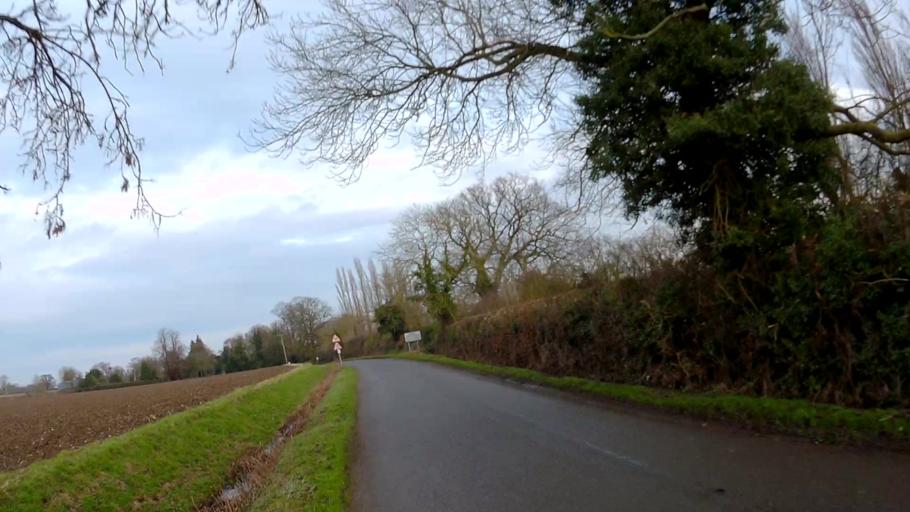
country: GB
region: England
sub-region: Lincolnshire
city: Bourne
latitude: 52.8313
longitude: -0.4133
